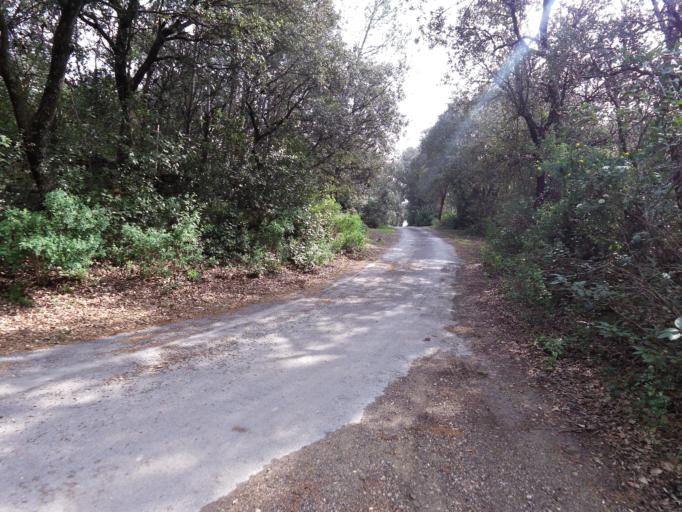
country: FR
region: Languedoc-Roussillon
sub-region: Departement du Gard
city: Aigues-Vives
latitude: 43.7476
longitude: 4.1668
